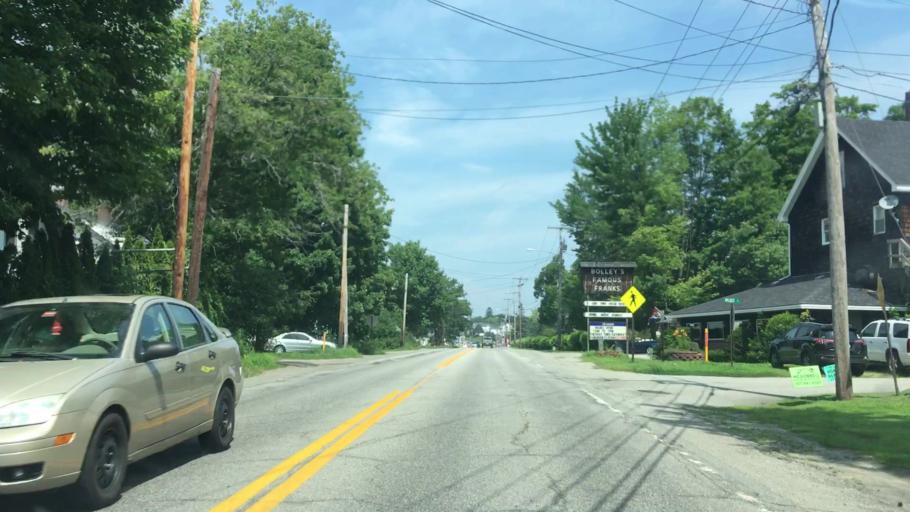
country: US
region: Maine
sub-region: Kennebec County
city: Hallowell
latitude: 44.2917
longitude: -69.7877
